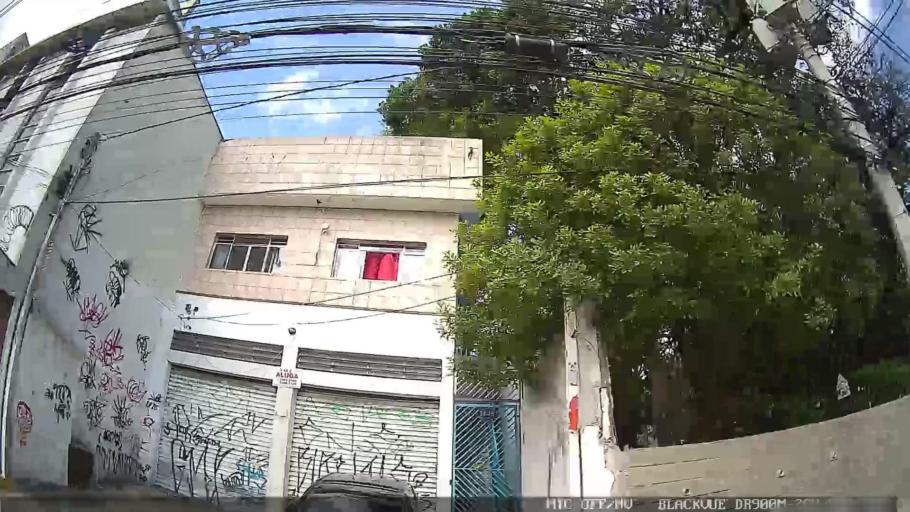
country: BR
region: Sao Paulo
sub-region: Guarulhos
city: Guarulhos
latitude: -23.4938
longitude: -46.4786
